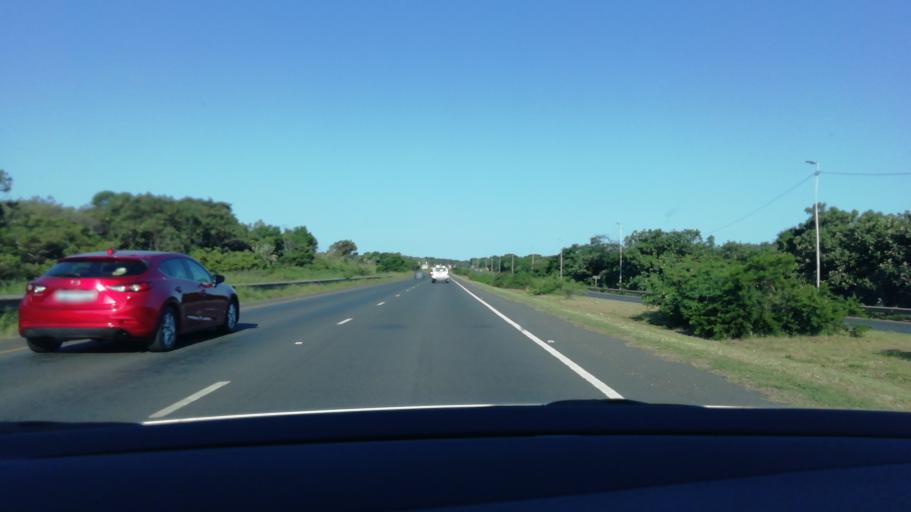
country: ZA
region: KwaZulu-Natal
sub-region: uThungulu District Municipality
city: Richards Bay
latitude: -28.7690
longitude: 32.0433
